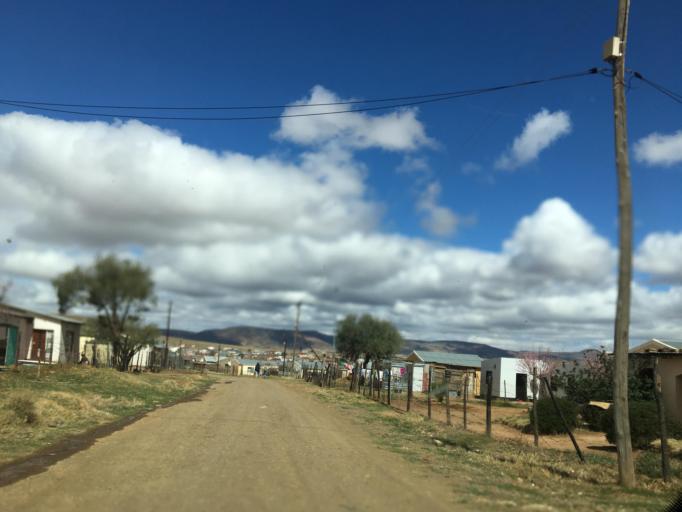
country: ZA
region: Eastern Cape
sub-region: Chris Hani District Municipality
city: Cala
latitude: -31.5309
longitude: 27.7036
